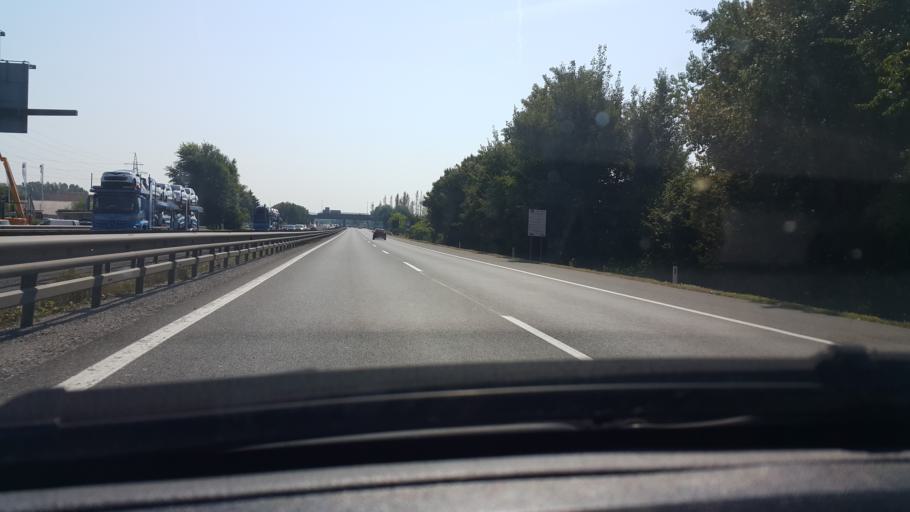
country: SI
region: Ljubljana
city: Ljubljana
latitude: 46.0332
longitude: 14.4694
